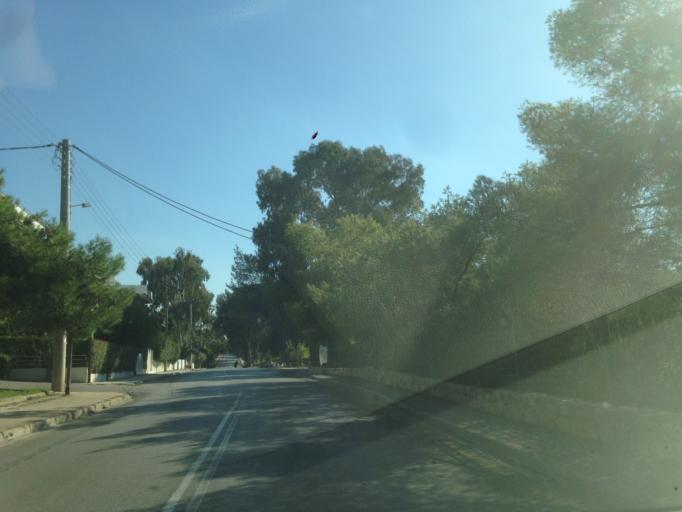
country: GR
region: Attica
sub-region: Nomarchia Anatolikis Attikis
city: Vouliagmeni
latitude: 37.8185
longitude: 23.7710
